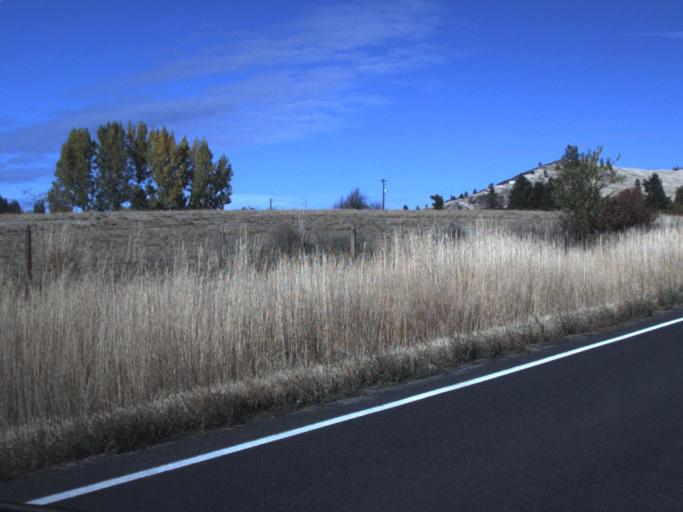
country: US
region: Washington
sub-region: Stevens County
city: Kettle Falls
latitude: 48.1497
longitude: -118.1747
